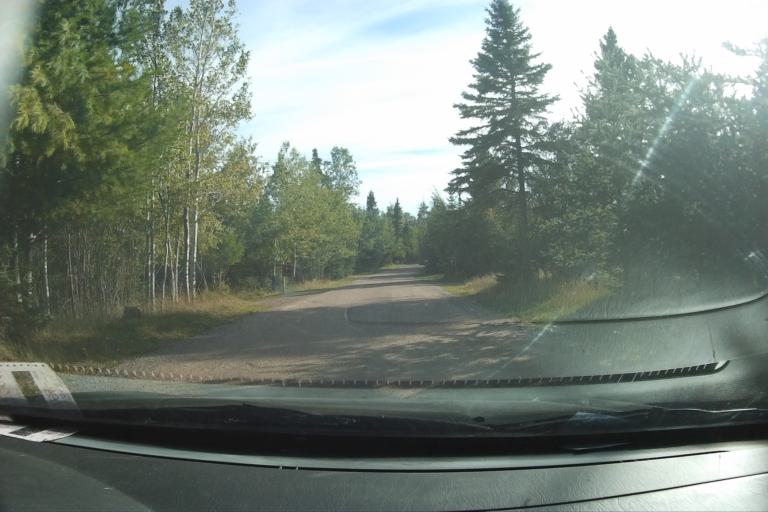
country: CA
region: Ontario
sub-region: Thunder Bay District
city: Thunder Bay
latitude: 48.3670
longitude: -88.8036
